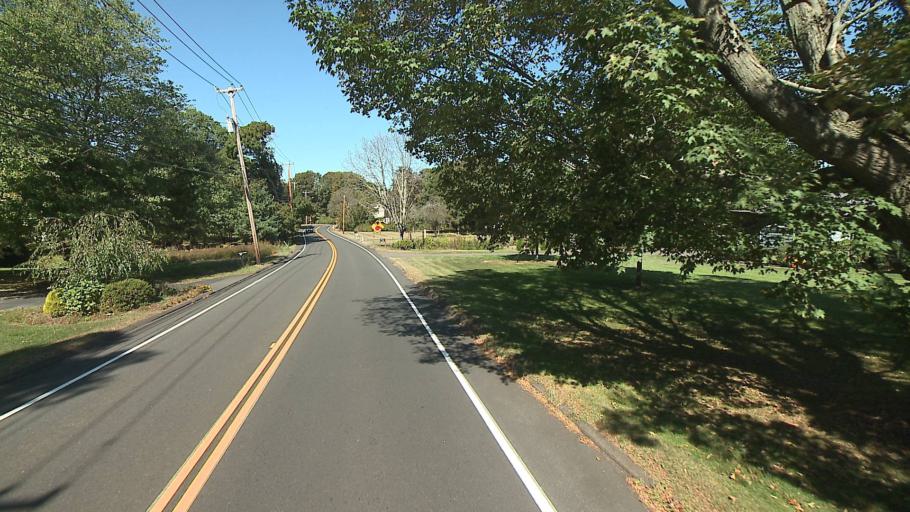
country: US
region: Connecticut
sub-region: New Haven County
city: Orange
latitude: 41.2869
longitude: -73.0299
